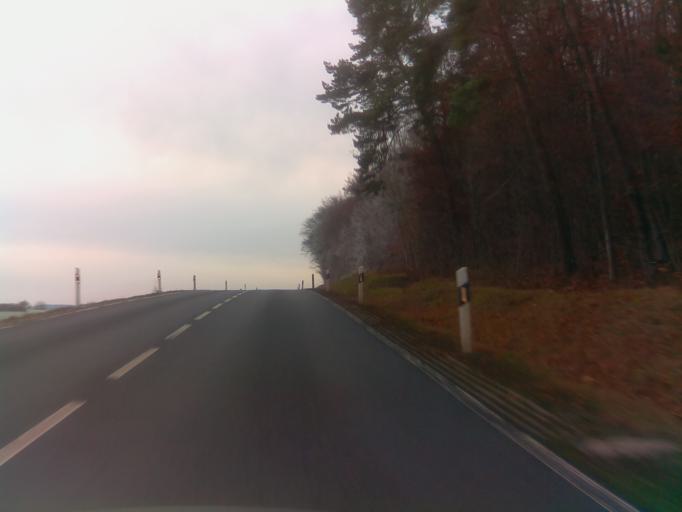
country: DE
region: Hesse
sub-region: Regierungsbezirk Kassel
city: Rasdorf
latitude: 50.7268
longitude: 9.9179
